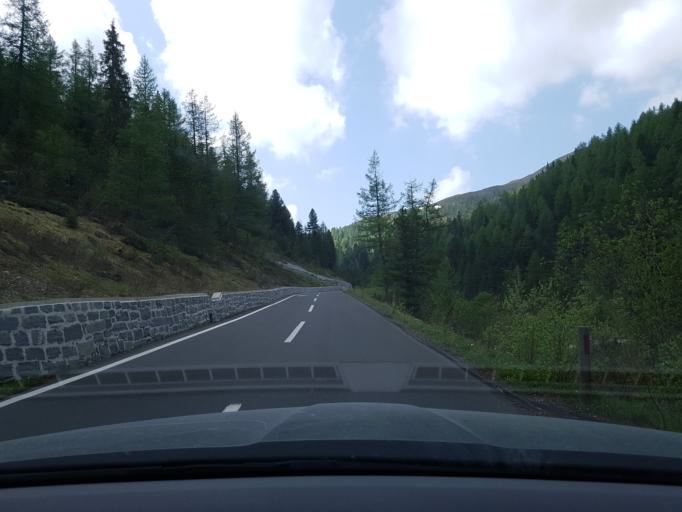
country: AT
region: Salzburg
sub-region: Politischer Bezirk Tamsweg
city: Thomatal
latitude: 46.9469
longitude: 13.7329
